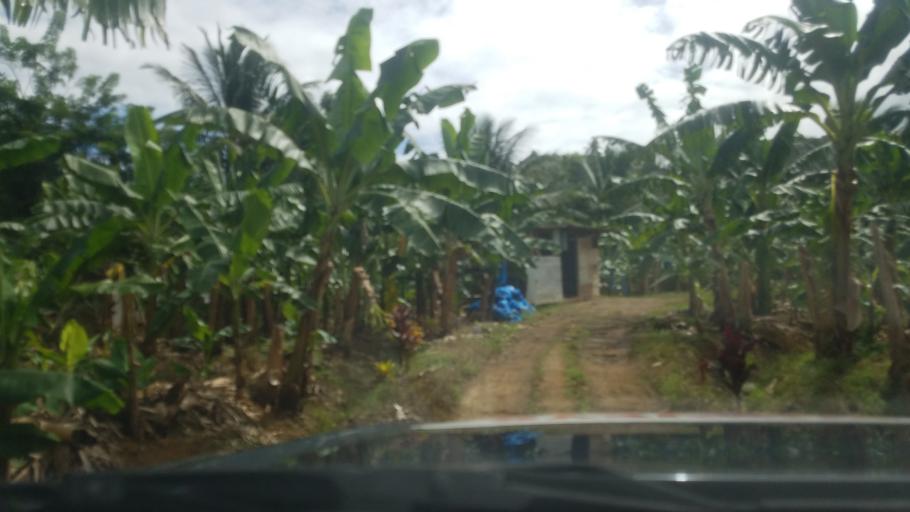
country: LC
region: Dennery Quarter
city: Dennery
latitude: 13.9318
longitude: -60.9248
